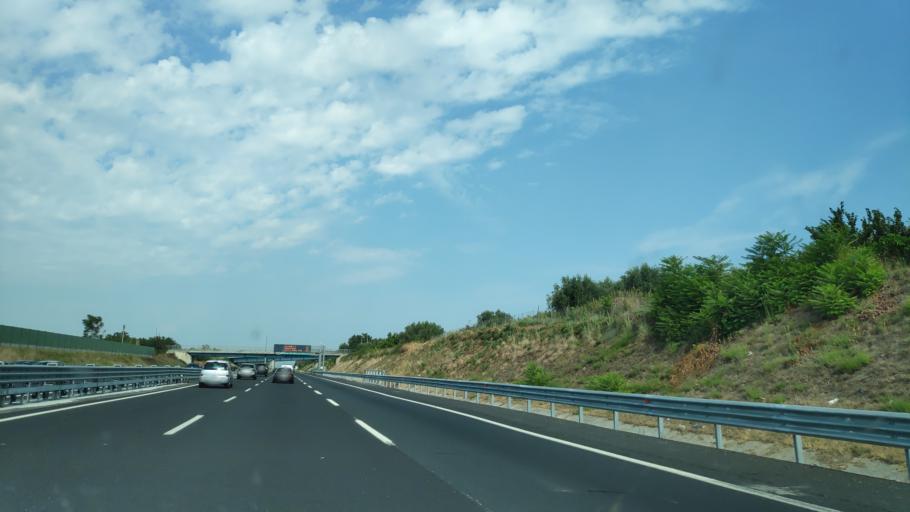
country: IT
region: Campania
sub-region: Provincia di Caserta
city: San Prisco
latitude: 41.0910
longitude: 14.2806
